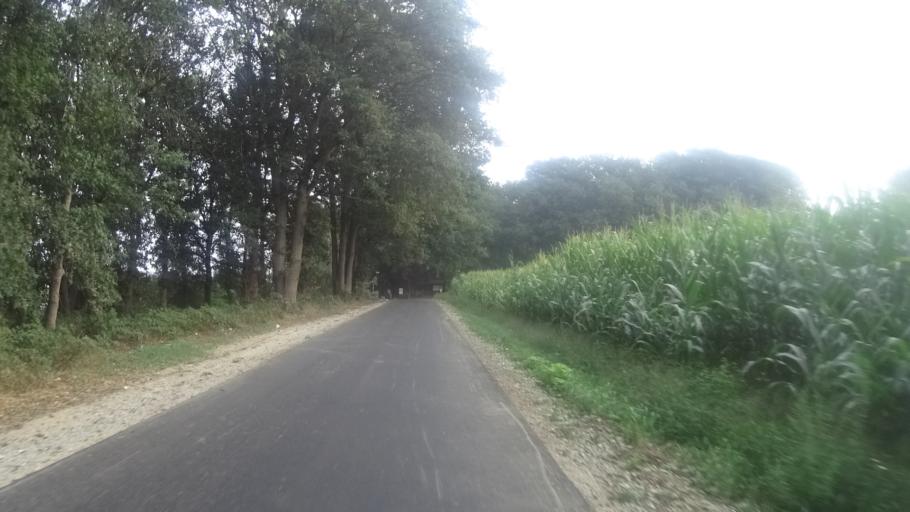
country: NL
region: Limburg
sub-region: Gemeente Venlo
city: Arcen
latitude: 51.4573
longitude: 6.1751
